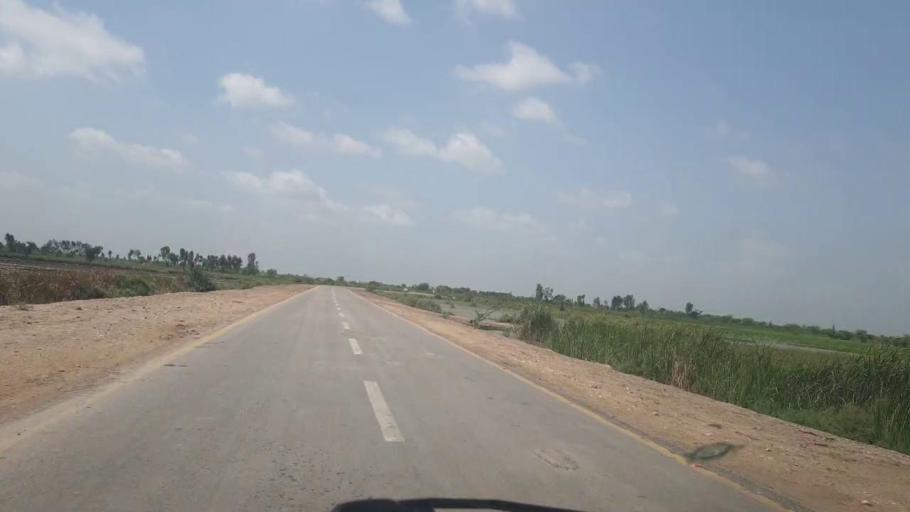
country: PK
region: Sindh
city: Berani
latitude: 25.6906
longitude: 68.9291
